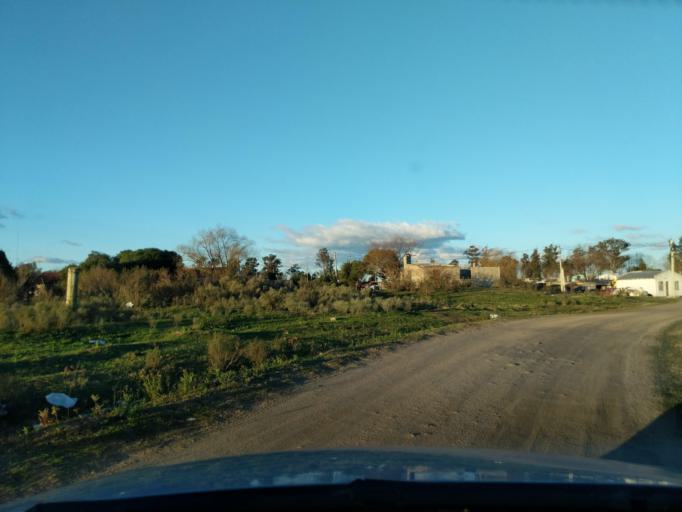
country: UY
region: Florida
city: Florida
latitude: -34.1028
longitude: -56.2388
